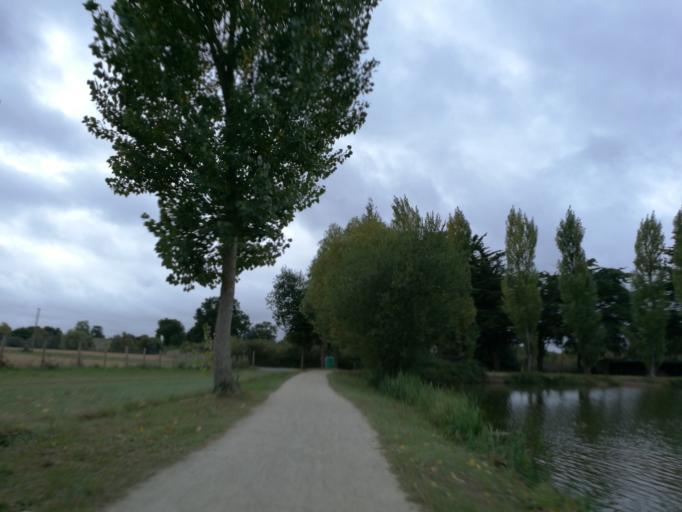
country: FR
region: Brittany
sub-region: Departement d'Ille-et-Vilaine
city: Bedee
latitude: 48.1663
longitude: -1.9540
